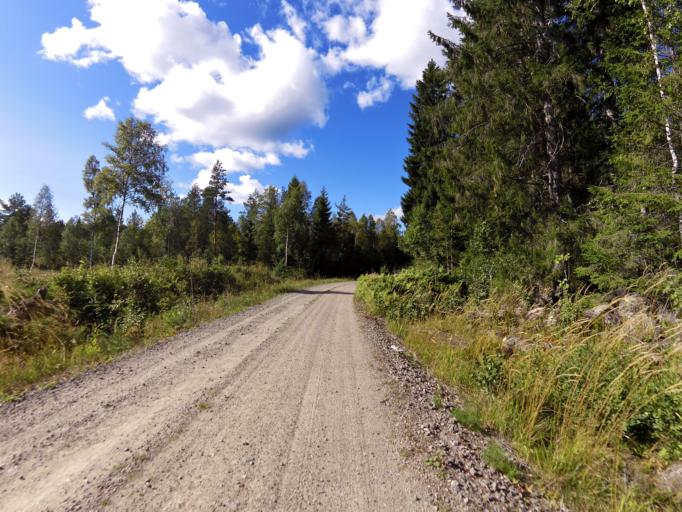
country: SE
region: Gaevleborg
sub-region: Ockelbo Kommun
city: Ockelbo
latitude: 60.8057
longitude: 16.8009
